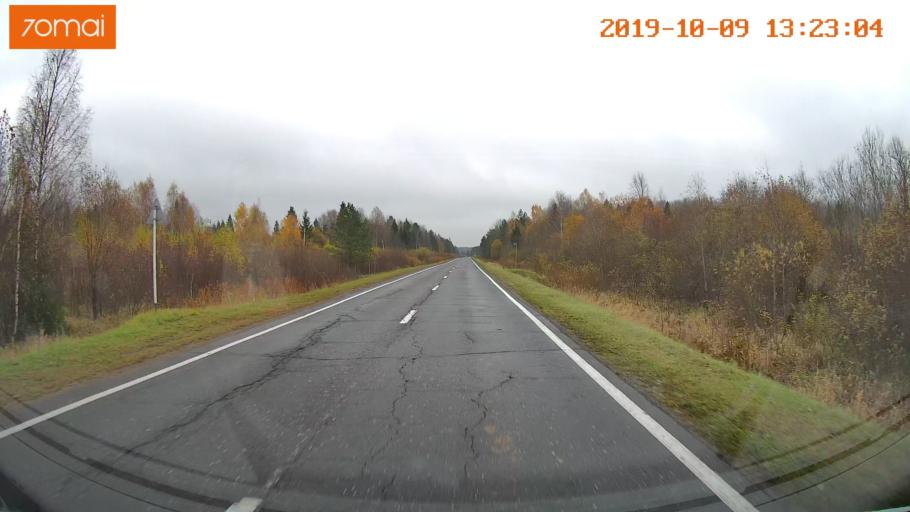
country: RU
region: Jaroslavl
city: Lyubim
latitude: 58.3370
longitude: 40.8800
